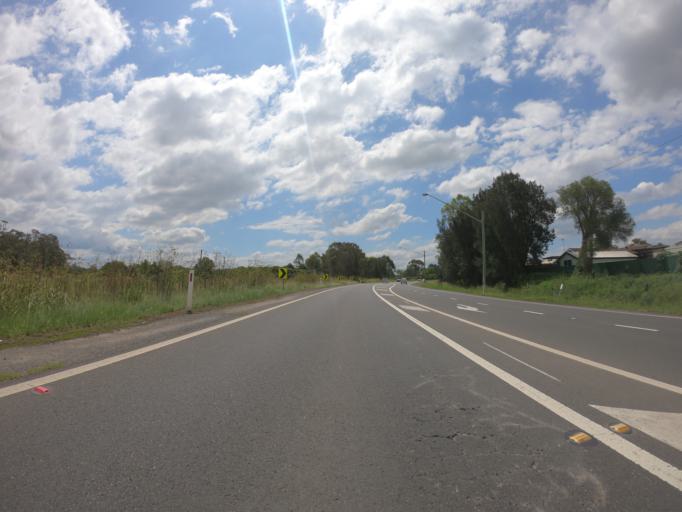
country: AU
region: New South Wales
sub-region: Blacktown
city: Mount Druitt
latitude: -33.8028
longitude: 150.7689
